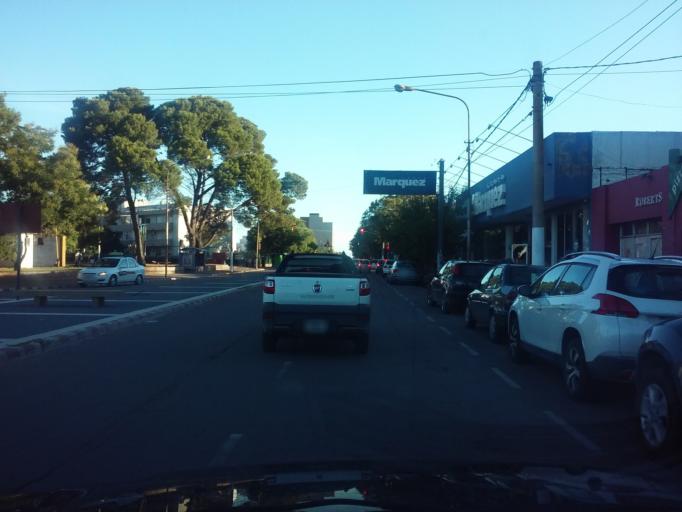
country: AR
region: La Pampa
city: Santa Rosa
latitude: -36.6212
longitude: -64.2814
